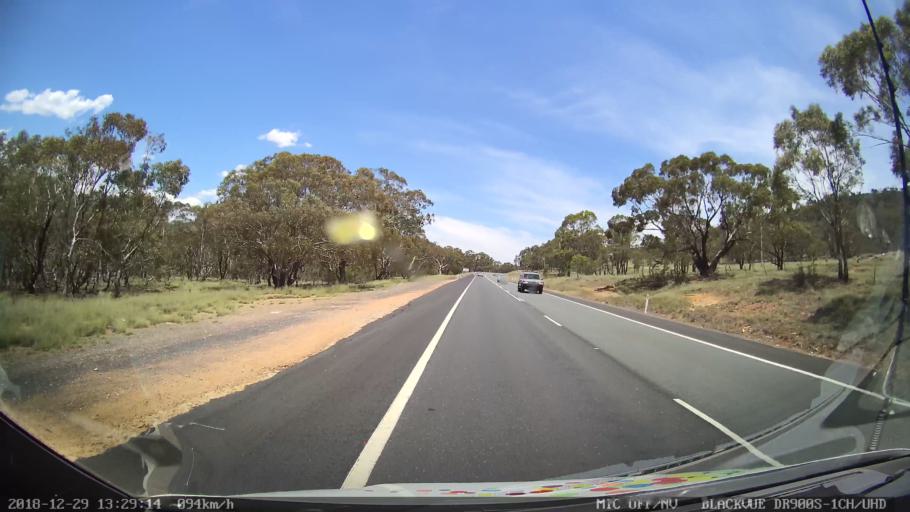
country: AU
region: New South Wales
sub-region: Cooma-Monaro
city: Cooma
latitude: -35.8872
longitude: 149.1616
